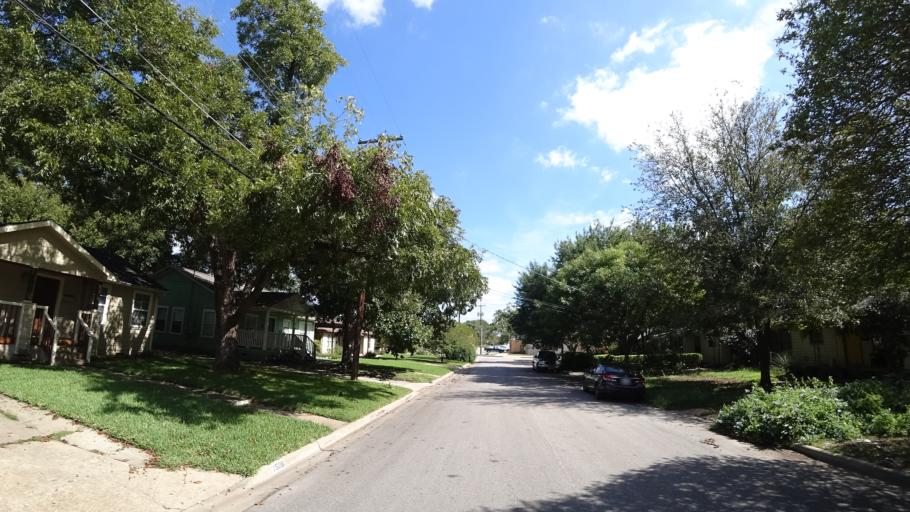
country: US
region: Texas
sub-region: Travis County
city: Austin
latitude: 30.3438
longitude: -97.7265
